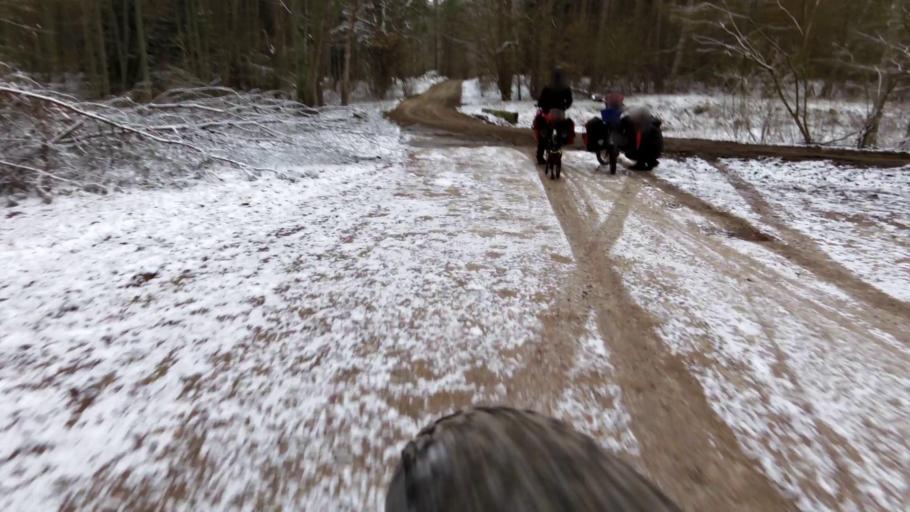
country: PL
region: West Pomeranian Voivodeship
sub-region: Powiat walecki
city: Miroslawiec
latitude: 53.3110
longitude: 16.0693
